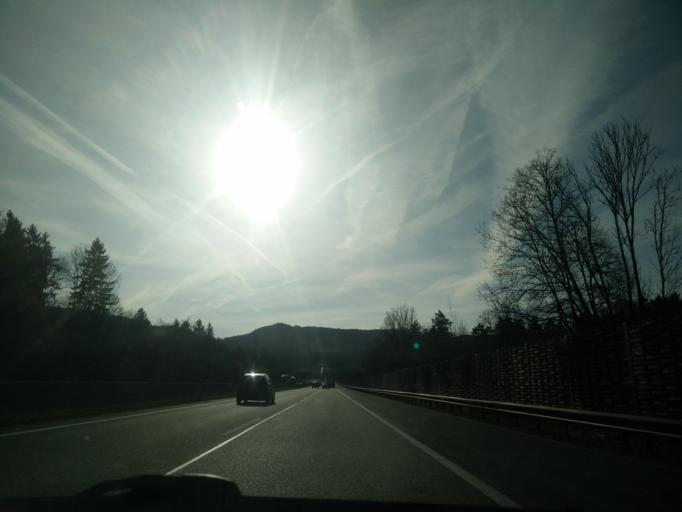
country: AT
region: Salzburg
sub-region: Politischer Bezirk Salzburg-Umgebung
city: Anif
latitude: 47.7337
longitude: 13.0744
